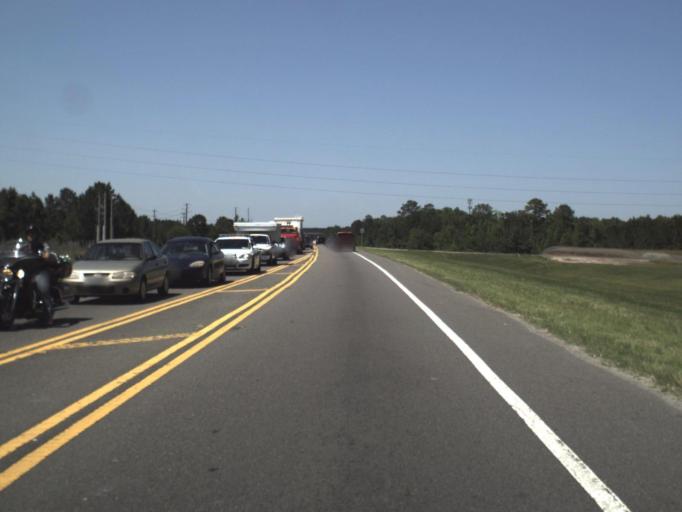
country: US
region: Florida
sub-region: Clay County
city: Lakeside
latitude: 30.1605
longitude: -81.8313
